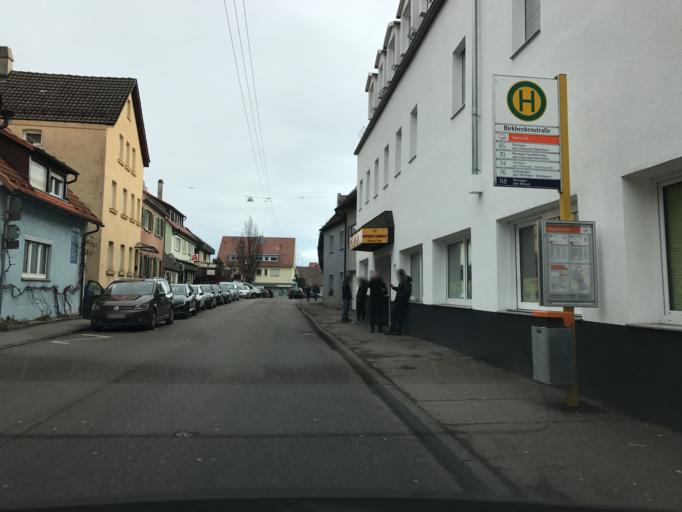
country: DE
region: Baden-Wuerttemberg
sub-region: Regierungsbezirk Stuttgart
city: Ostfildern
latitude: 48.7231
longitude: 9.2079
